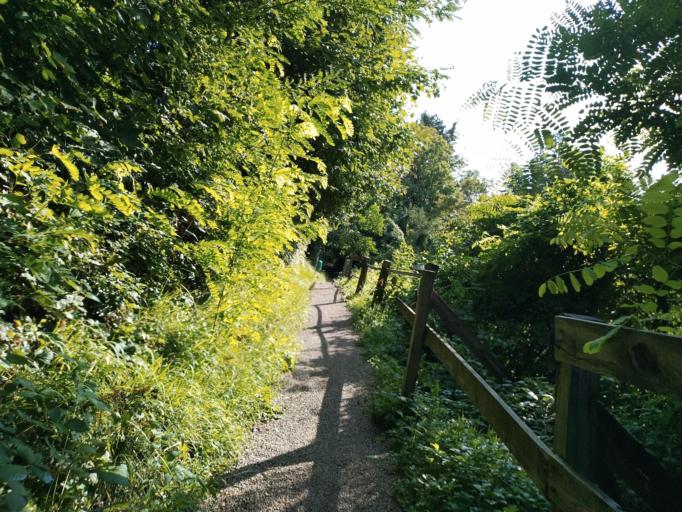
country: AT
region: Lower Austria
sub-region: Politischer Bezirk Wien-Umgebung
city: Pressbaum
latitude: 48.1822
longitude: 16.0799
